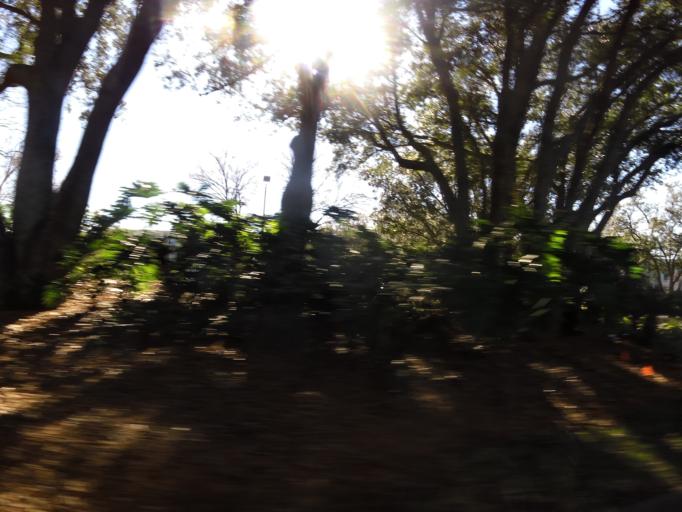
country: US
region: Florida
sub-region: Duval County
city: Jacksonville
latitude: 30.2601
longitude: -81.6022
